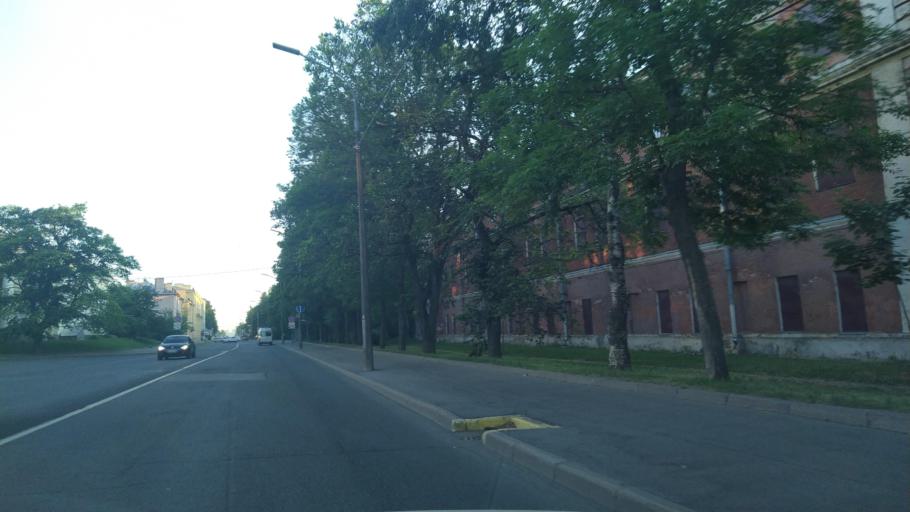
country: RU
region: St.-Petersburg
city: Kronshtadt
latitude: 60.0006
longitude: 29.7619
